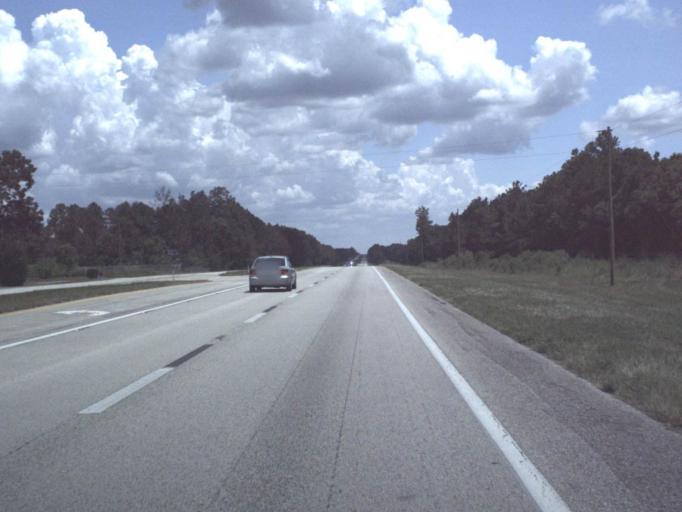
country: US
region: Florida
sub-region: Alachua County
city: Waldo
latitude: 29.6937
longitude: -82.1300
